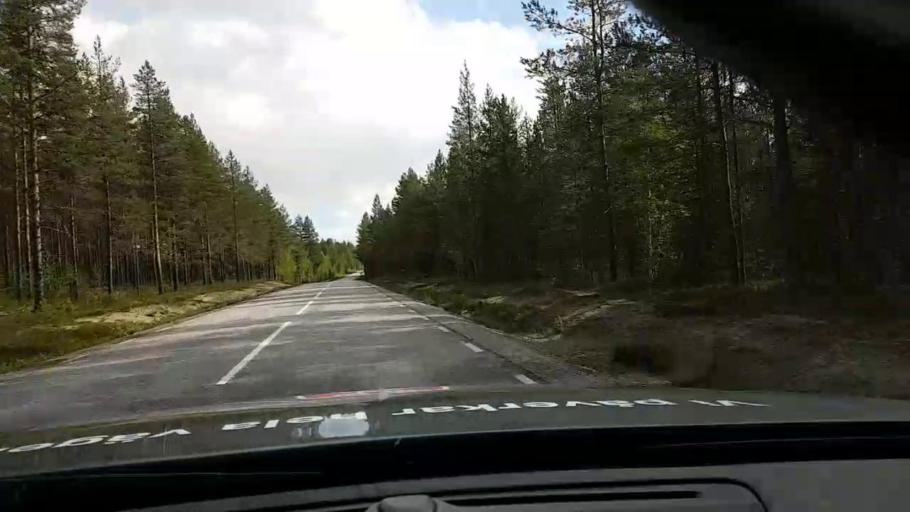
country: SE
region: Vaesternorrland
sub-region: OErnskoeldsviks Kommun
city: Bredbyn
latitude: 63.6520
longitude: 17.8880
